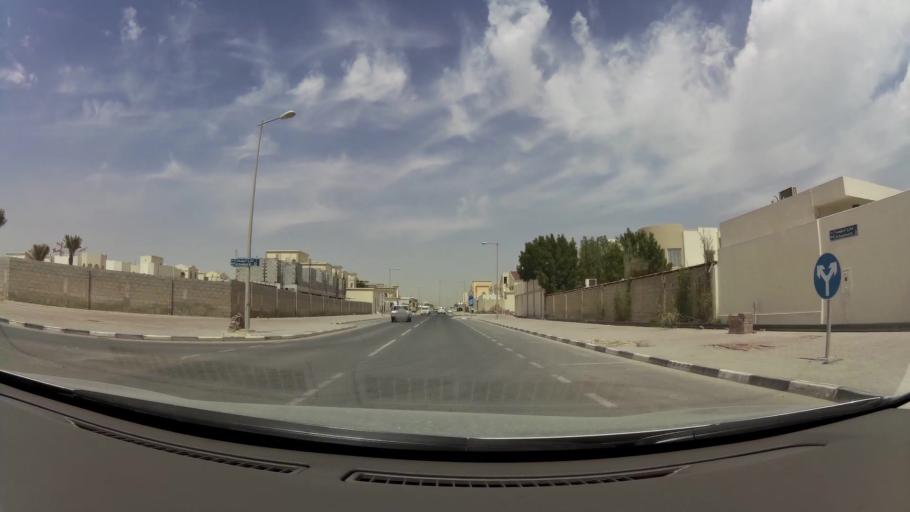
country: QA
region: Baladiyat ar Rayyan
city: Ar Rayyan
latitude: 25.2569
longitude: 51.4263
